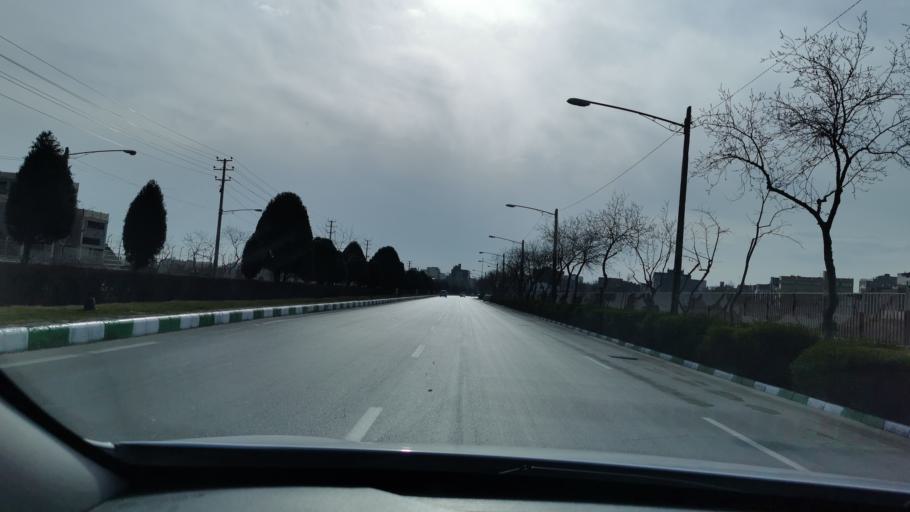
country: IR
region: Razavi Khorasan
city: Mashhad
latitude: 36.3009
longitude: 59.5202
